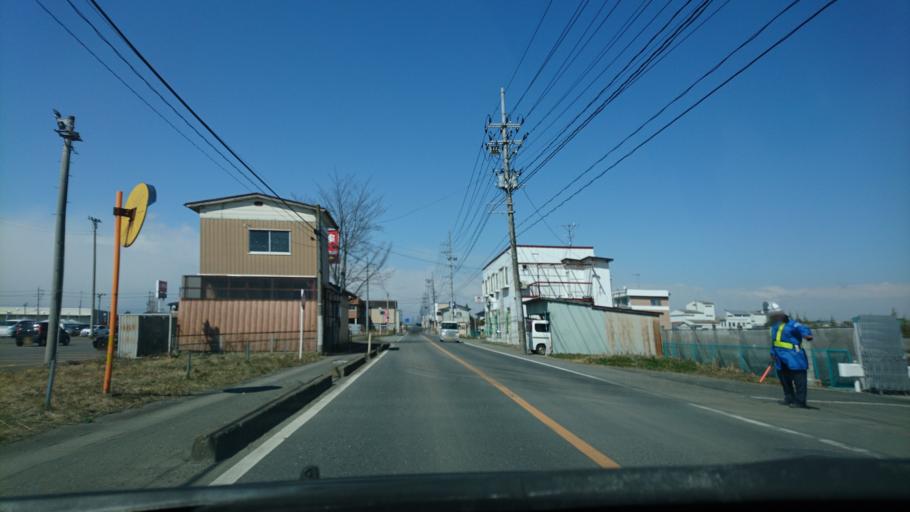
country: JP
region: Iwate
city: Ichinoseki
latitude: 38.7704
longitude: 141.1498
